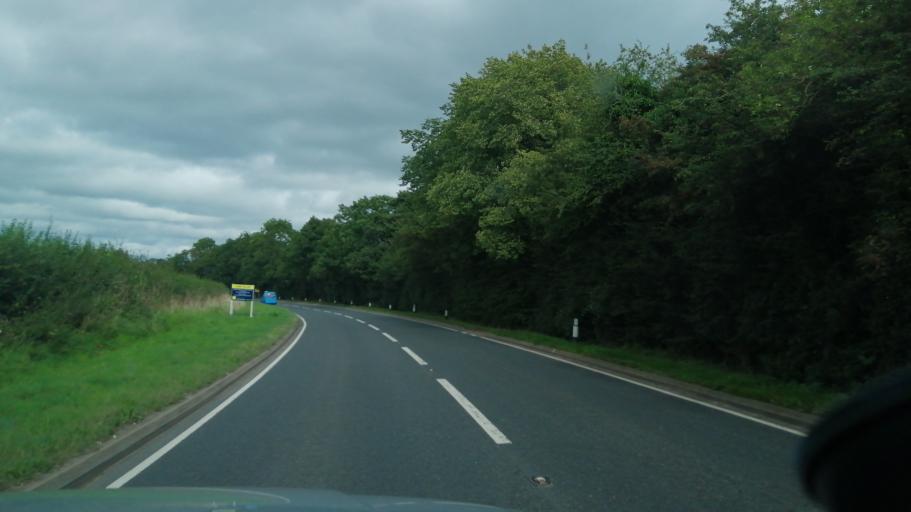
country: GB
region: Wales
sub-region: Monmouthshire
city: Grosmont
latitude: 51.9568
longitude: -2.8575
